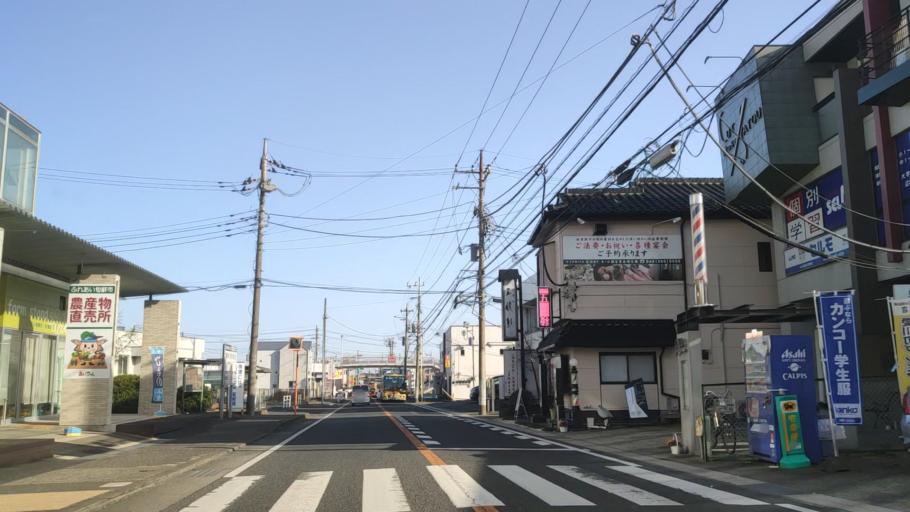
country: JP
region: Kanagawa
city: Zama
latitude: 35.5144
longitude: 139.3362
